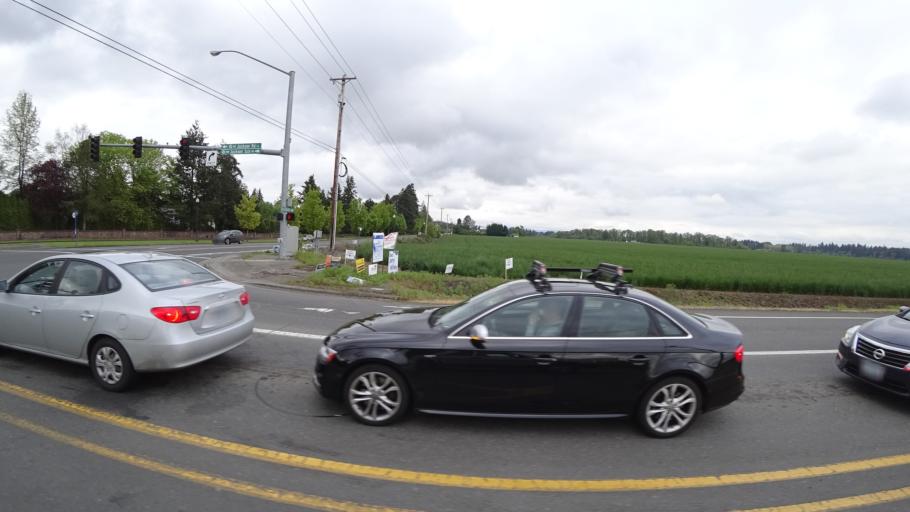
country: US
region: Oregon
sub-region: Washington County
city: Hillsboro
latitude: 45.5502
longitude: -122.9735
